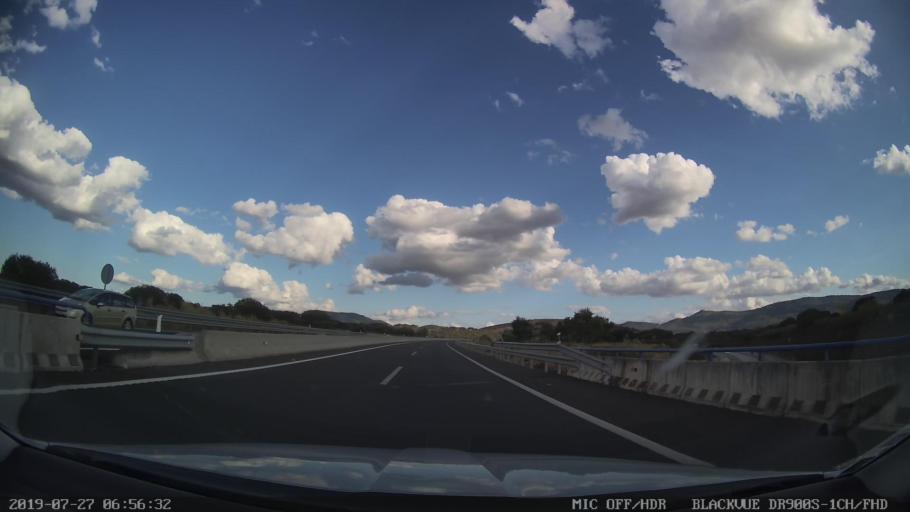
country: ES
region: Extremadura
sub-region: Provincia de Caceres
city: Casas de Miravete
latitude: 39.7674
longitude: -5.7355
